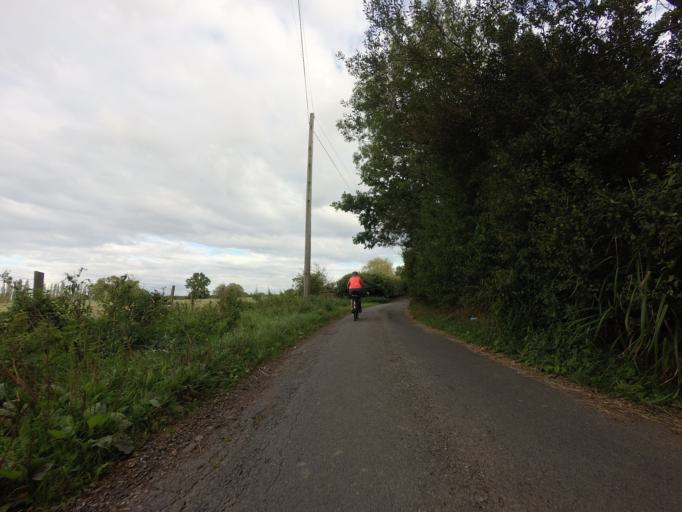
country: GB
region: England
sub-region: Kent
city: Staplehurst
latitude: 51.1993
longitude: 0.5732
